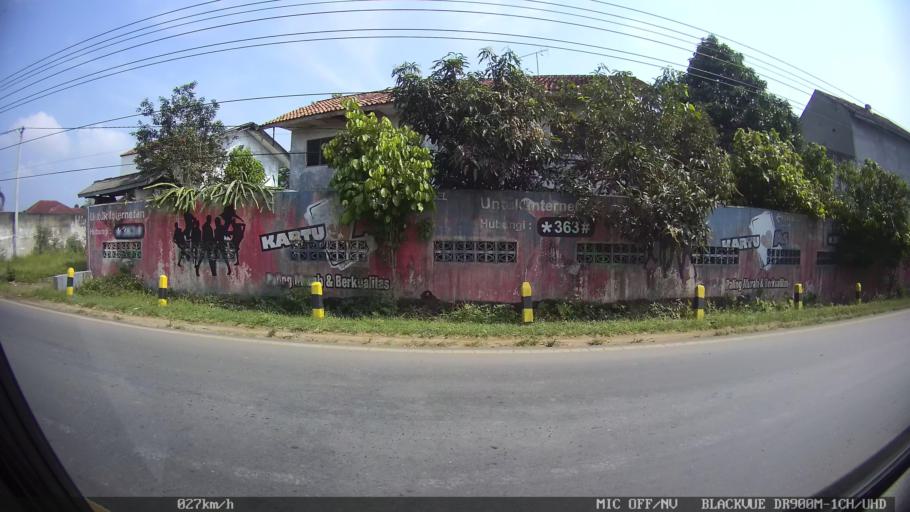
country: ID
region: Lampung
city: Gadingrejo
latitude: -5.3698
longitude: 105.0543
